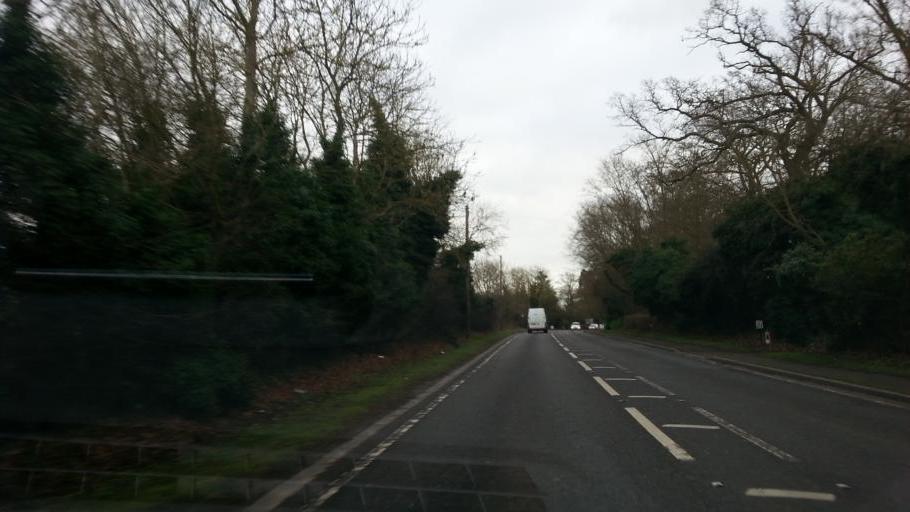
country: GB
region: England
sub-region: Cambridgeshire
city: Linton
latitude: 52.1232
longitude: 0.2348
